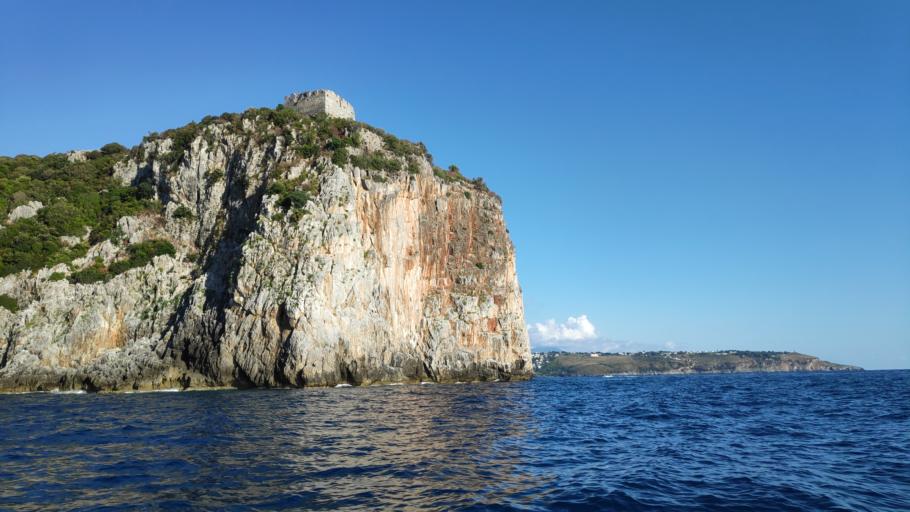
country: IT
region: Calabria
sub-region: Provincia di Cosenza
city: Praia a Mare
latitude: 39.8734
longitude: 15.7680
